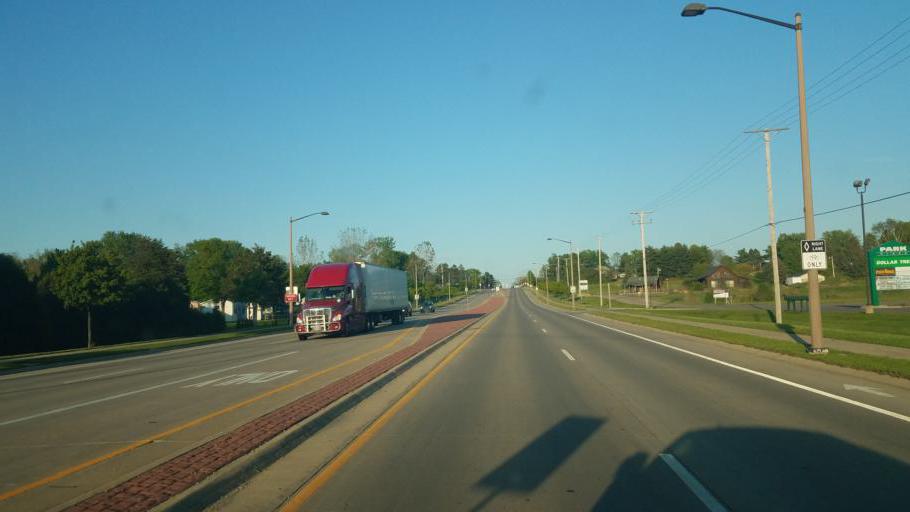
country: US
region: Wisconsin
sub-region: Sauk County
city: Reedsburg
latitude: 43.5325
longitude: -89.9693
